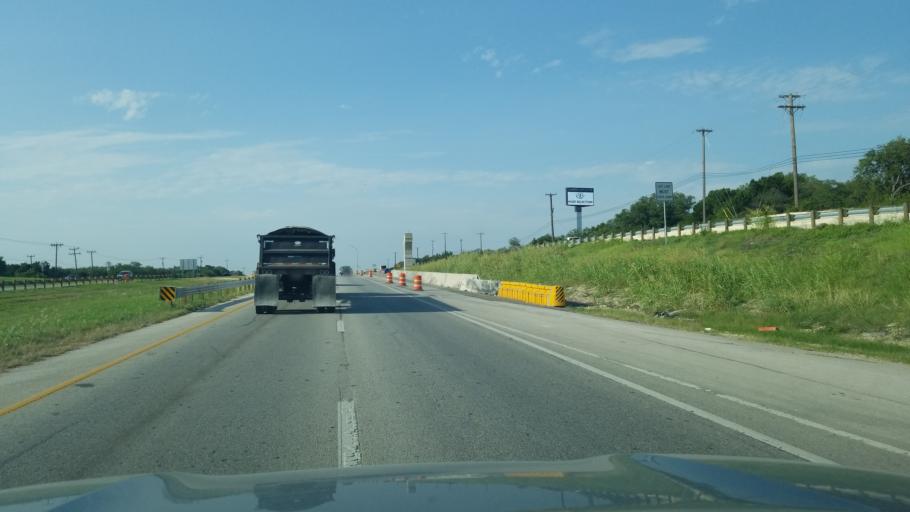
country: US
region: Texas
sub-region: Bexar County
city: Leon Valley
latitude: 29.4791
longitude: -98.7108
